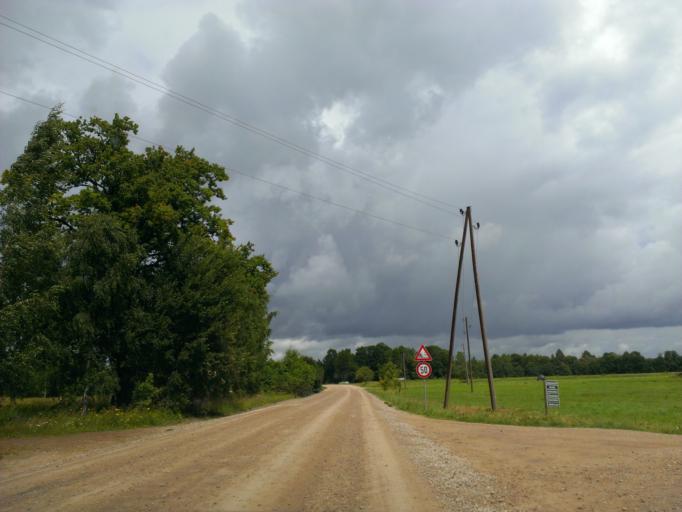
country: LV
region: Sigulda
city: Sigulda
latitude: 57.1956
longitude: 24.9454
